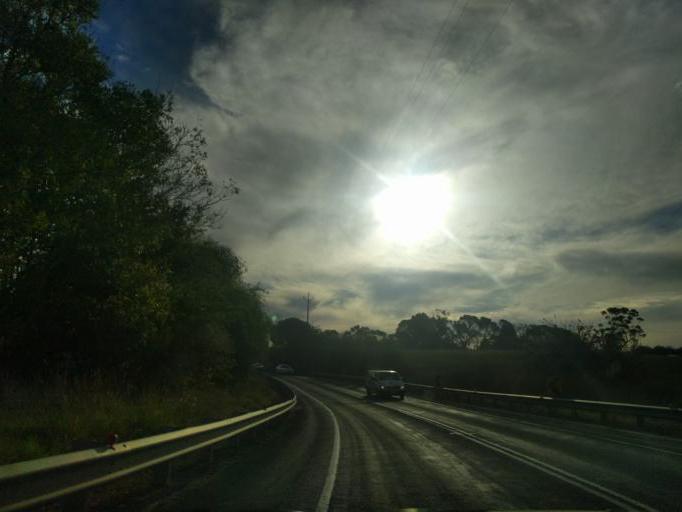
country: AU
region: South Australia
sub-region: Mount Barker
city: Little Hampton
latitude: -35.0443
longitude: 138.8331
